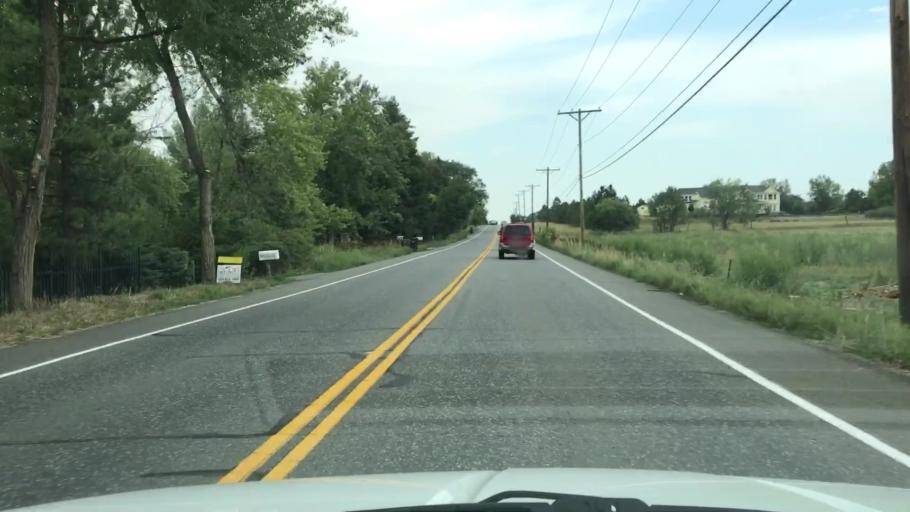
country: US
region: Colorado
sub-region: Boulder County
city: Louisville
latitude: 40.0001
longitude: -105.1485
